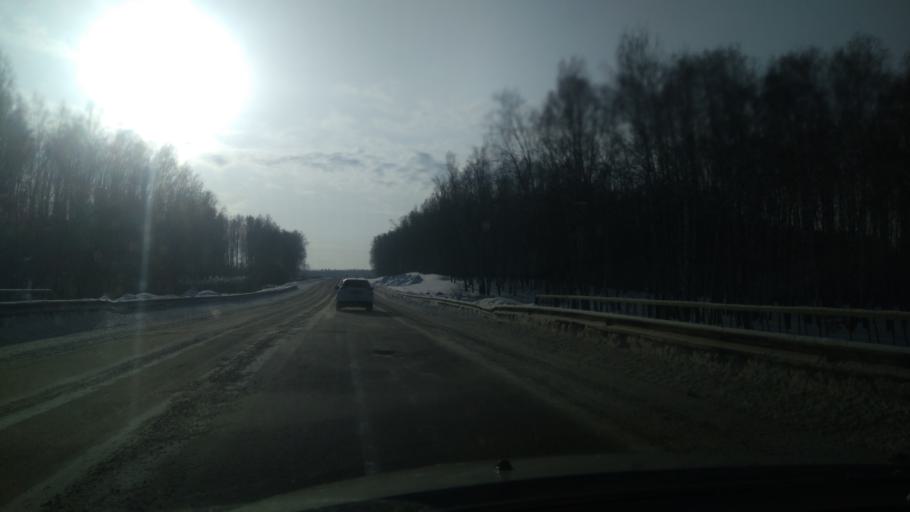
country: RU
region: Sverdlovsk
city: Bogdanovich
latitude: 56.7874
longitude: 61.9995
